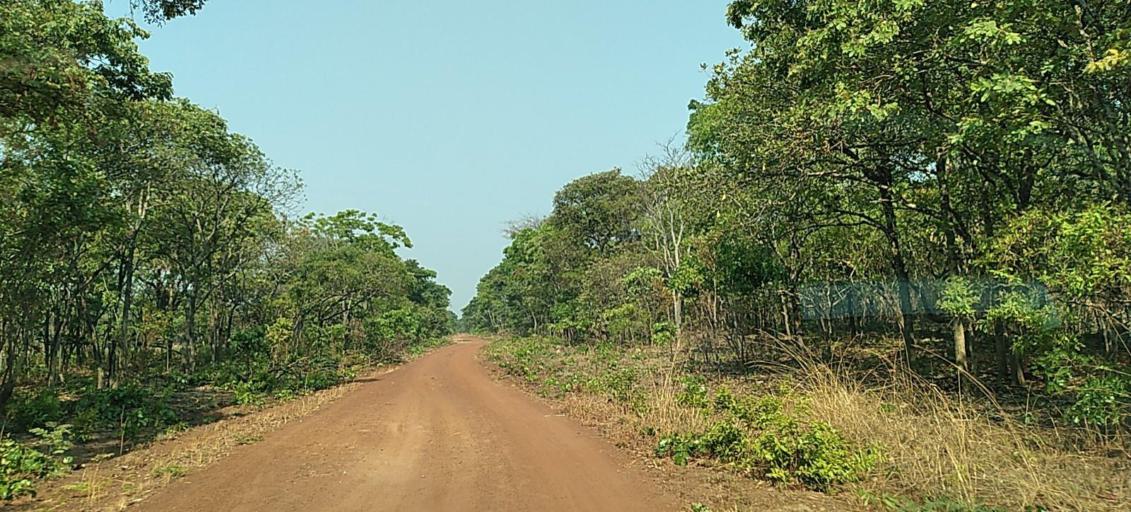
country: ZM
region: Copperbelt
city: Chingola
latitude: -12.8796
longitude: 27.4392
